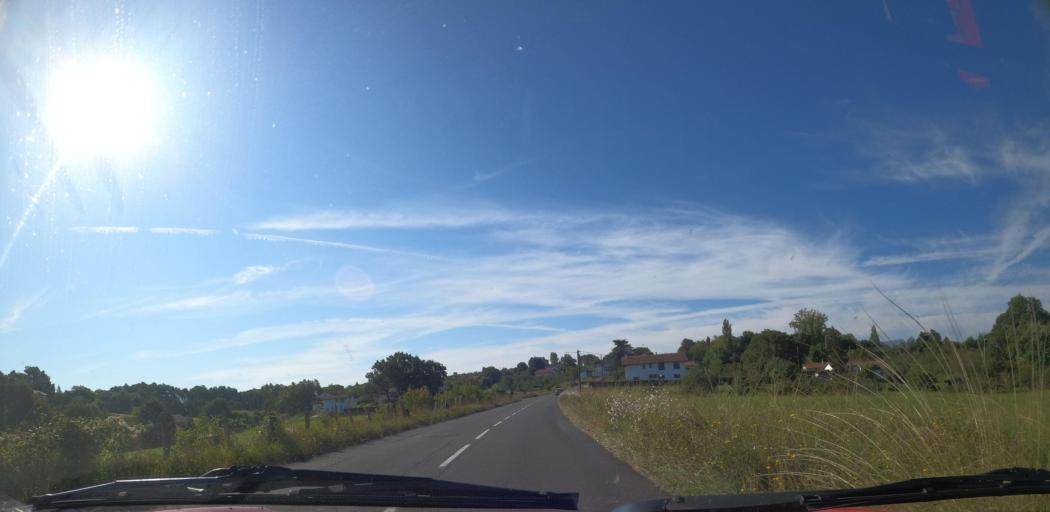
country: FR
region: Aquitaine
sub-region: Departement des Pyrenees-Atlantiques
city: Arbonne
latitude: 43.4144
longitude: -1.5476
